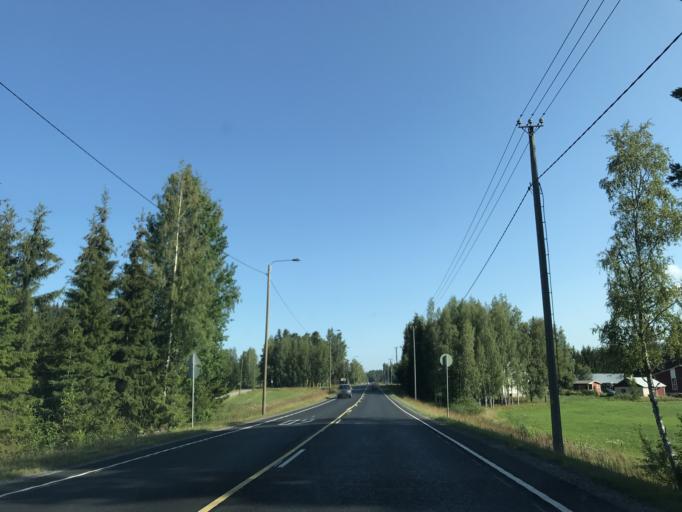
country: FI
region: Paijanne Tavastia
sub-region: Lahti
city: Lahti
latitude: 61.0540
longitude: 25.6694
